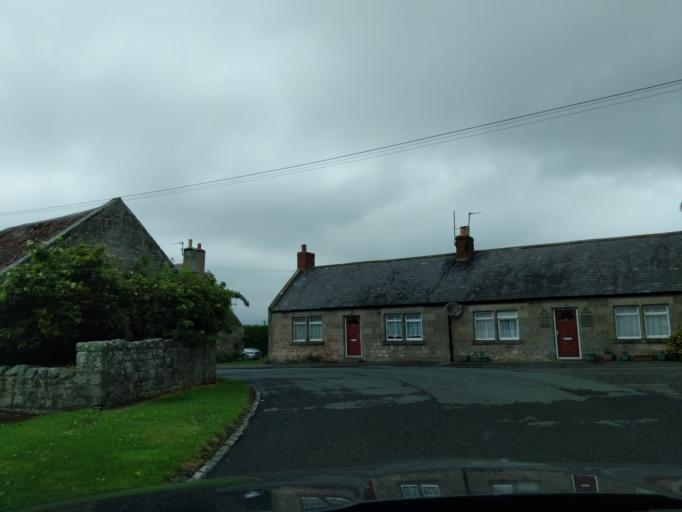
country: GB
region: England
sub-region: Northumberland
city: Ford
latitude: 55.6966
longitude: -2.1365
